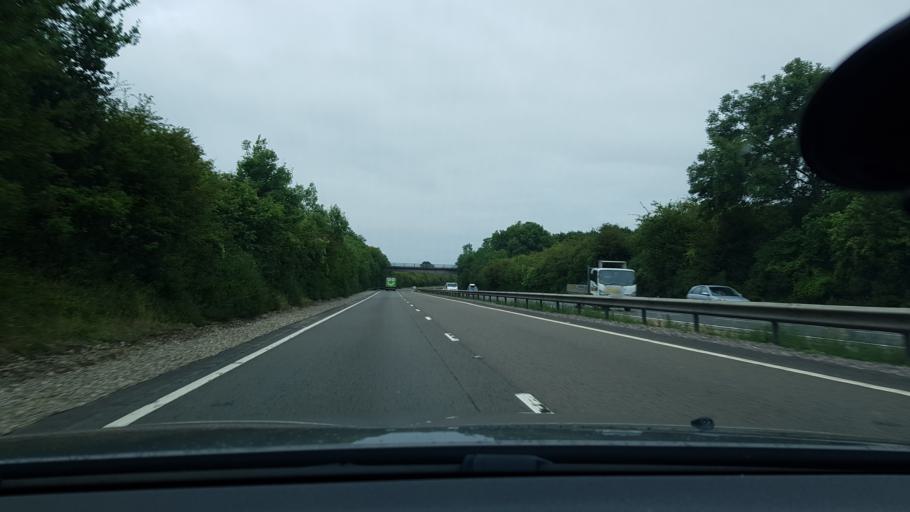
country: GB
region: England
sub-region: Hampshire
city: Overton
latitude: 51.2503
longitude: -1.3406
